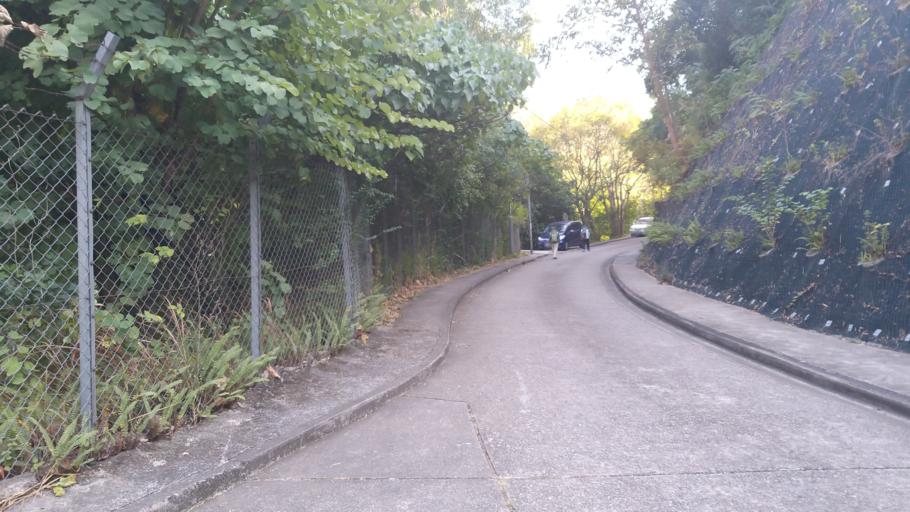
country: HK
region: Tuen Mun
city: Tuen Mun
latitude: 22.4076
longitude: 113.9853
